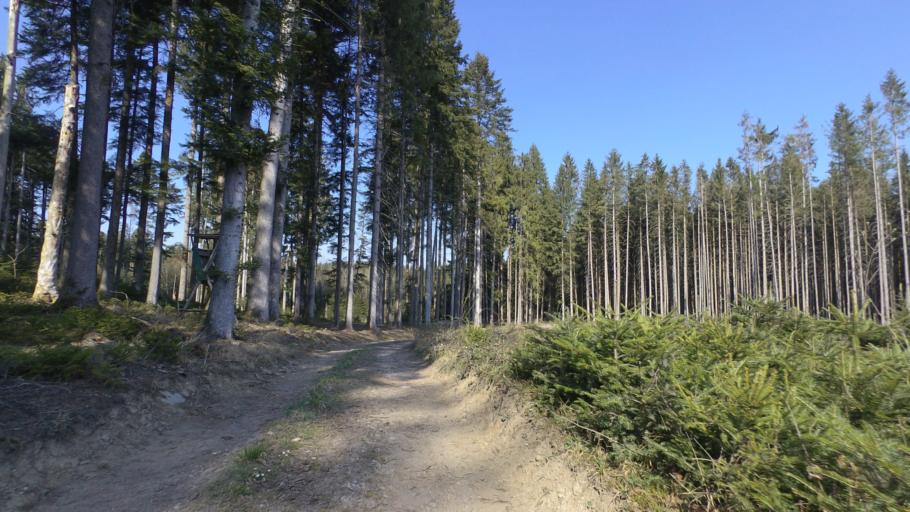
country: DE
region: Bavaria
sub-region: Upper Bavaria
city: Traunreut
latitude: 47.9347
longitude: 12.5808
